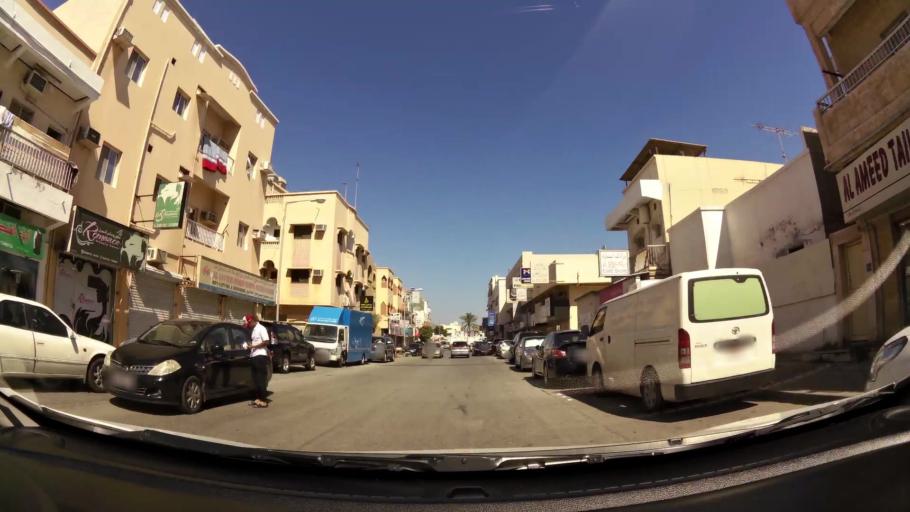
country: BH
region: Muharraq
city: Al Muharraq
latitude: 26.2573
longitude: 50.6190
